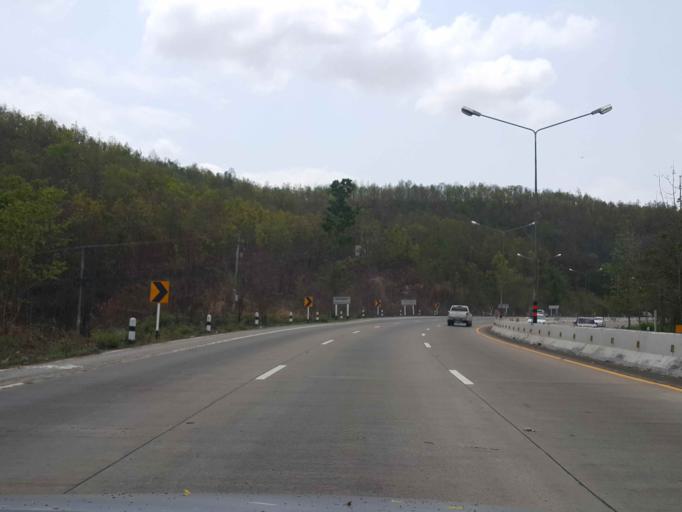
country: TH
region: Lamphun
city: Mae Tha
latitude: 18.4947
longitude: 99.1353
